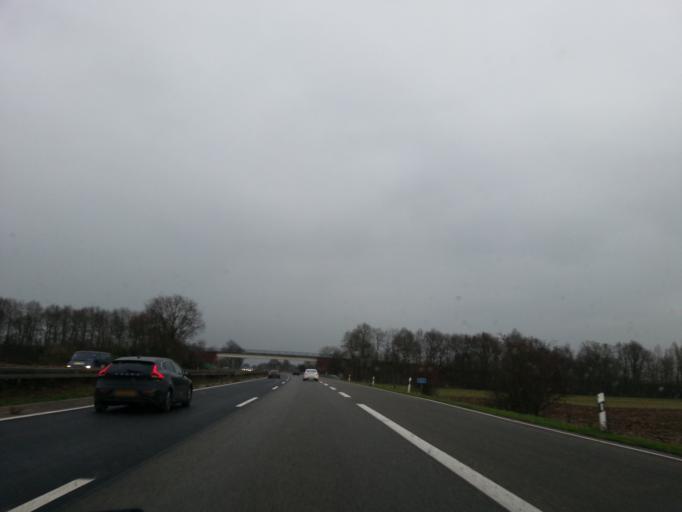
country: NL
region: Gelderland
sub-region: Gemeente Montferland
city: s-Heerenberg
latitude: 51.8458
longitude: 6.3101
